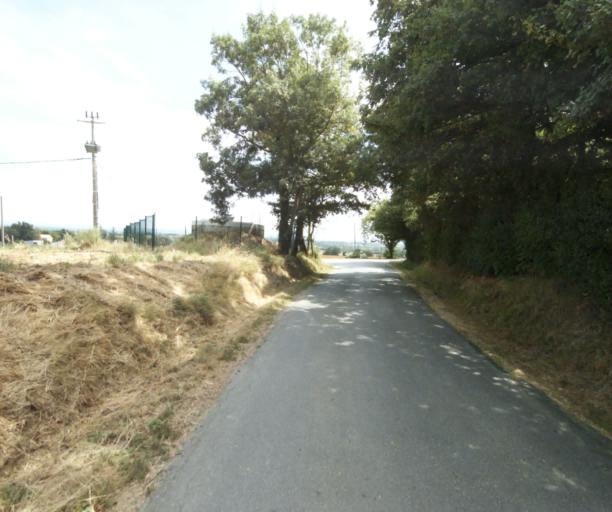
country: FR
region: Midi-Pyrenees
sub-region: Departement du Tarn
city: Dourgne
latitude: 43.5060
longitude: 2.0915
